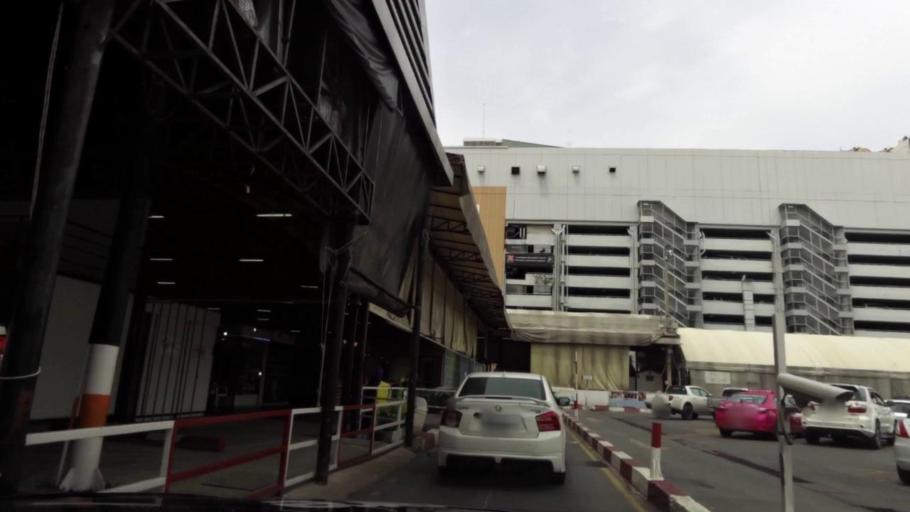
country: TH
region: Bangkok
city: Bang Kapi
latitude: 13.7652
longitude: 100.6412
